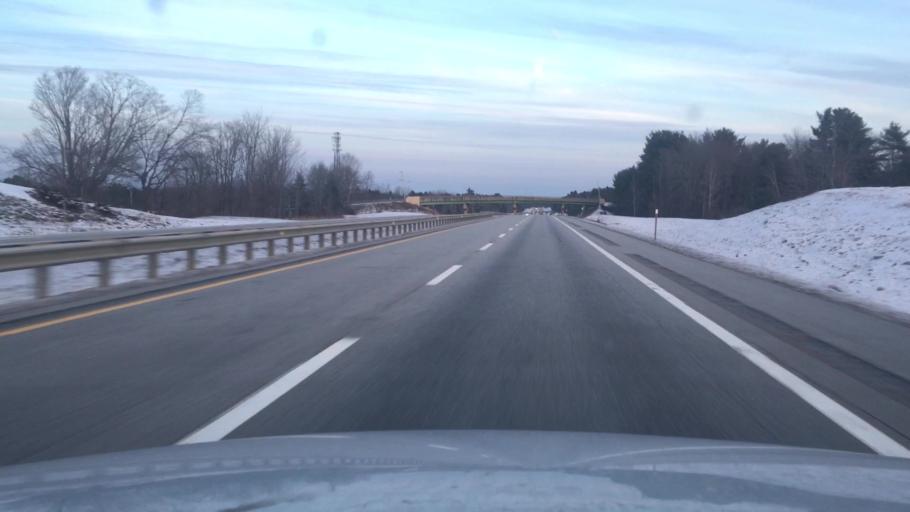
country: US
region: Maine
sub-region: Sagadahoc County
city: Richmond
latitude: 44.1471
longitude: -69.9190
